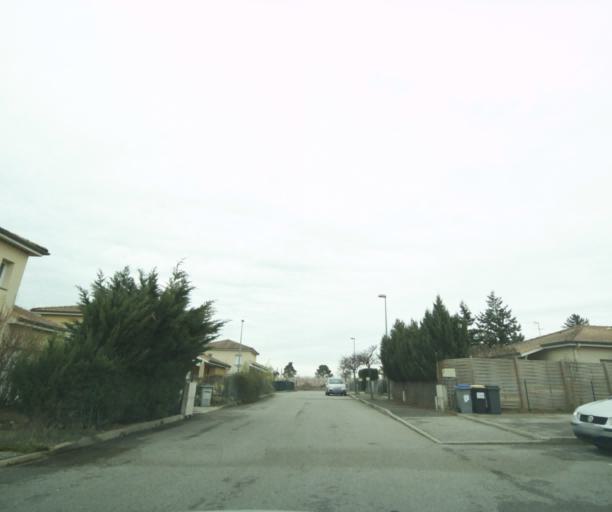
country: FR
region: Rhone-Alpes
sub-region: Departement de la Drome
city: Bourg-les-Valence
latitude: 44.9654
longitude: 4.8903
